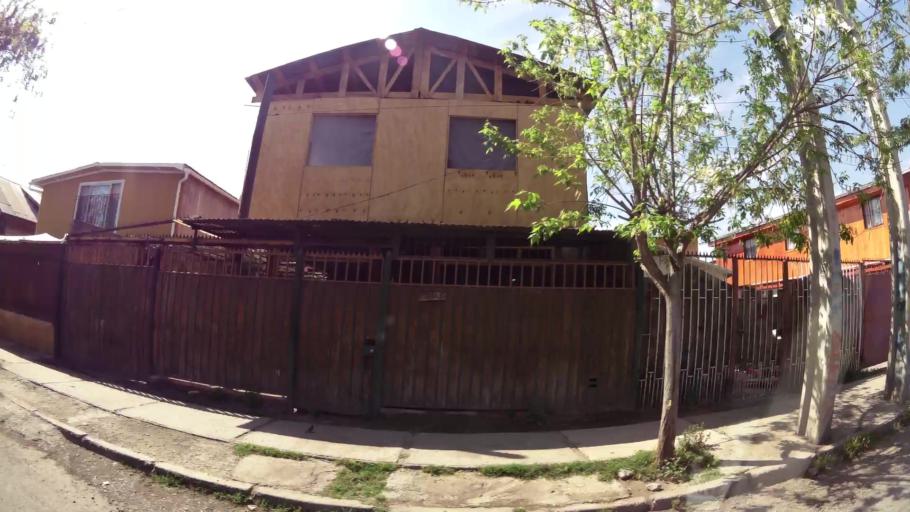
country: CL
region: Santiago Metropolitan
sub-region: Provincia de Santiago
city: La Pintana
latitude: -33.5578
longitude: -70.6498
